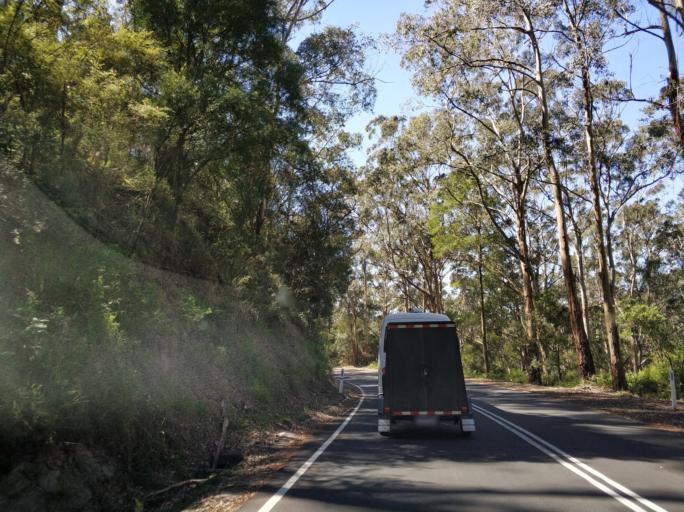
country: AU
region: Victoria
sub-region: Colac-Otway
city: Apollo Bay
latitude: -38.7402
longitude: 143.2522
